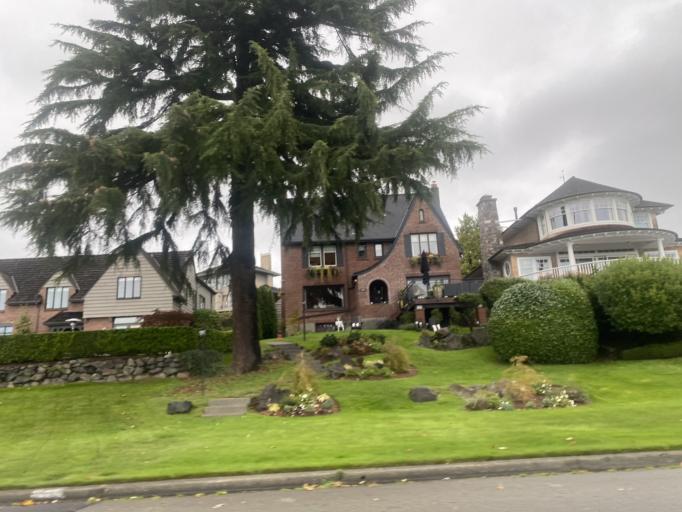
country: US
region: Washington
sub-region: King County
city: Seattle
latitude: 47.6375
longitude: -122.4076
